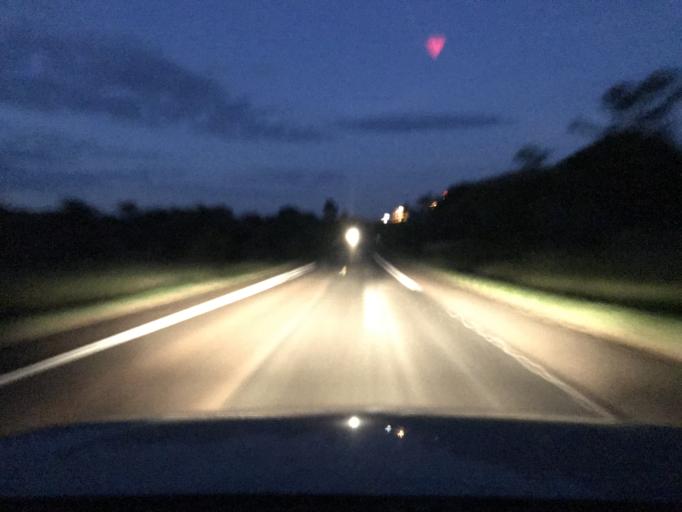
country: PY
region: Canindeyu
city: Salto del Guaira
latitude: -24.1043
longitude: -54.2344
